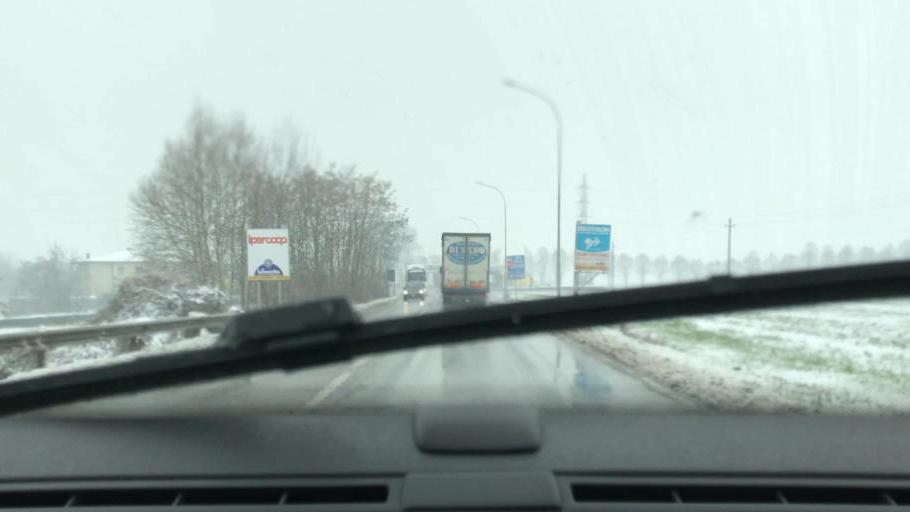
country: IT
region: Lombardy
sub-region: Provincia di Mantova
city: Goito
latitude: 45.2598
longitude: 10.6632
